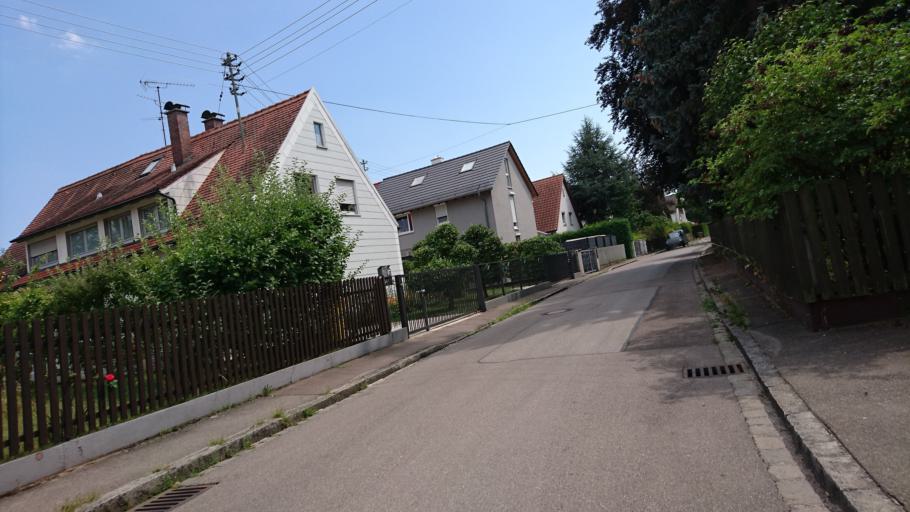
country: DE
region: Bavaria
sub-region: Swabia
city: Augsburg
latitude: 48.3907
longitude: 10.9270
